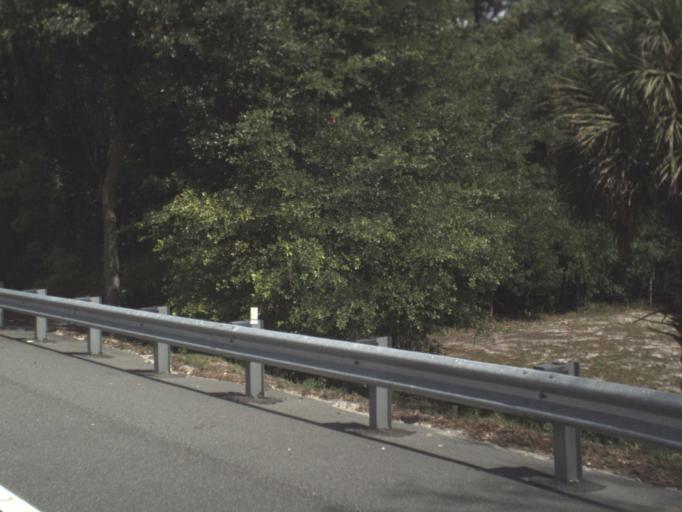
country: US
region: Florida
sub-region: Putnam County
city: Interlachen
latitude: 29.7273
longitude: -81.9259
